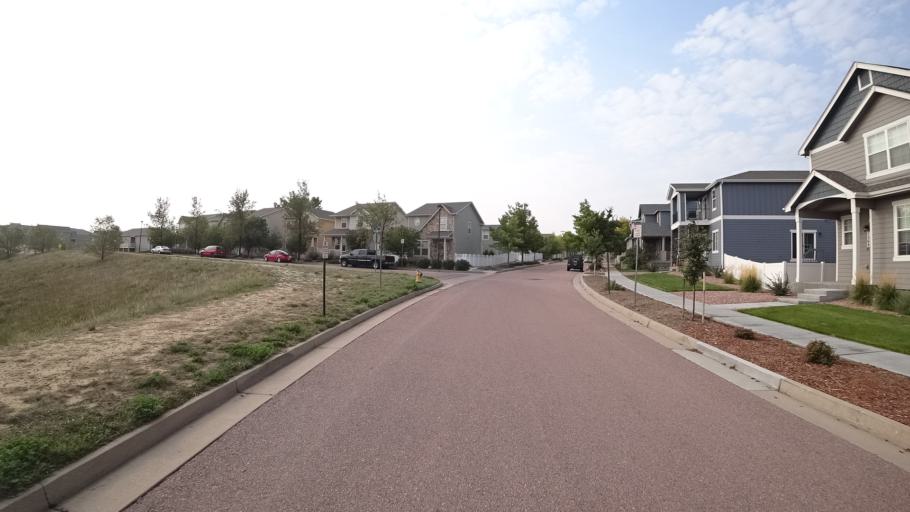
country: US
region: Colorado
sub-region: El Paso County
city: Stratmoor
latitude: 38.8113
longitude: -104.7856
